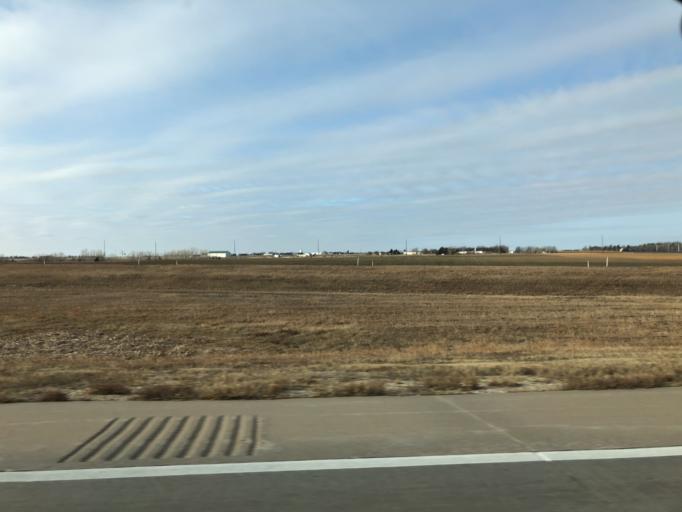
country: US
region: Kansas
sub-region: Reno County
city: South Hutchinson
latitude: 38.0171
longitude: -97.9683
